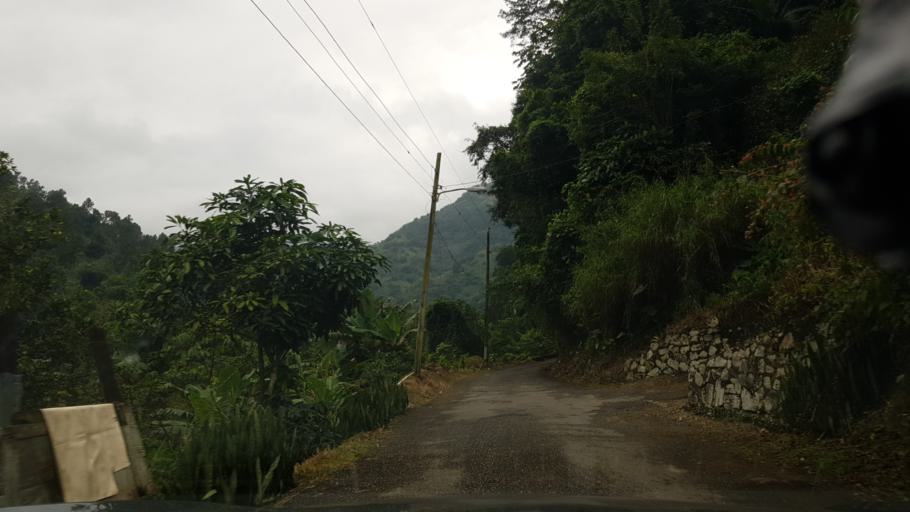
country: JM
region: Saint Andrew
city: Stony Hill
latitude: 18.1219
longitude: -76.7153
